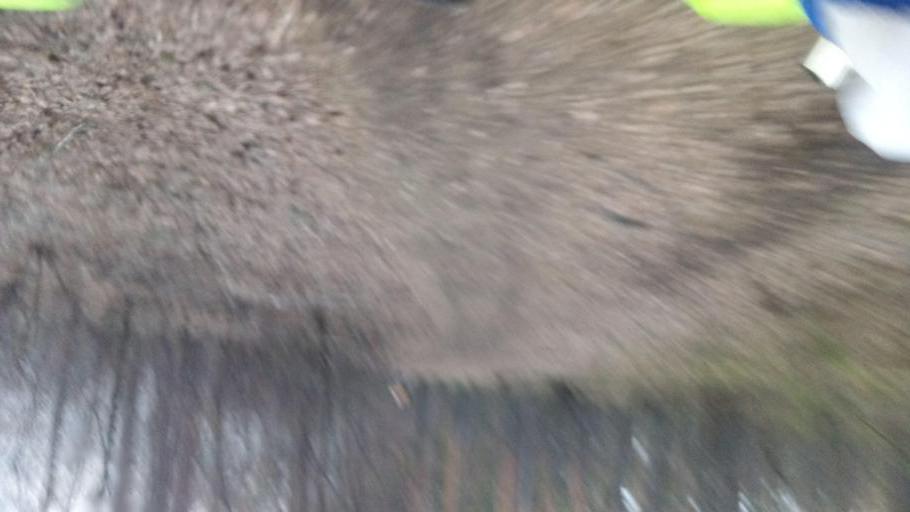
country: RU
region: Chelyabinsk
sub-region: Gorod Chelyabinsk
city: Chelyabinsk
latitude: 55.1653
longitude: 61.3229
